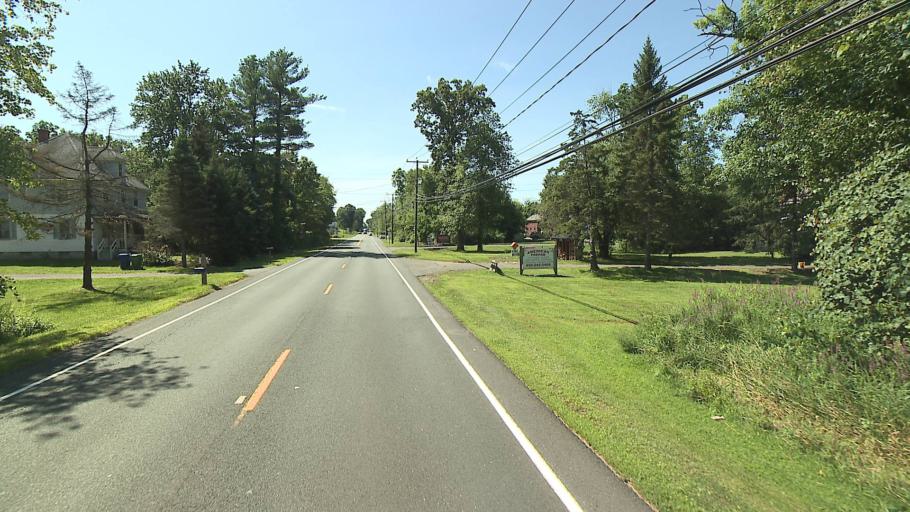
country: US
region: Connecticut
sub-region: Hartford County
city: Blue Hills
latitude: 41.8450
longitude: -72.7005
